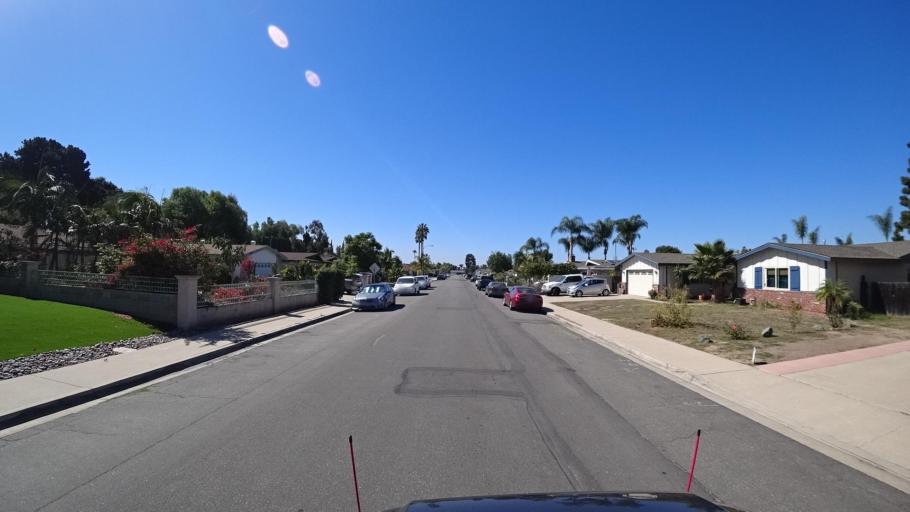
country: US
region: California
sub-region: San Diego County
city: Bonita
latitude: 32.6684
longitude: -117.0179
